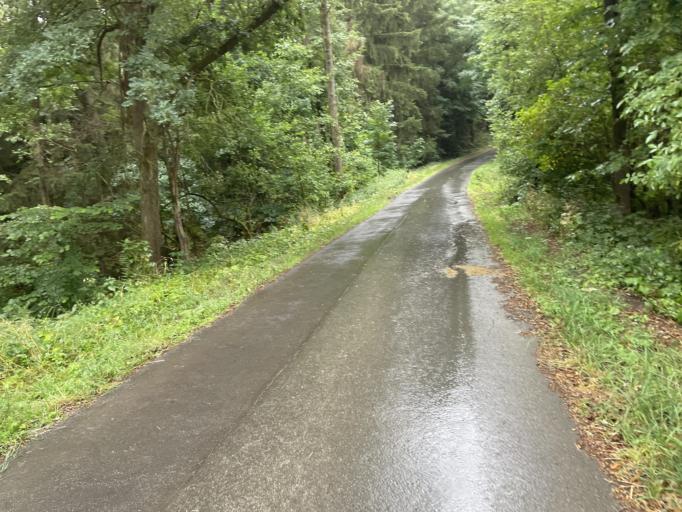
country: DE
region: Bavaria
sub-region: Upper Franconia
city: Neunkirchen am Main
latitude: 49.9377
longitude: 11.6391
